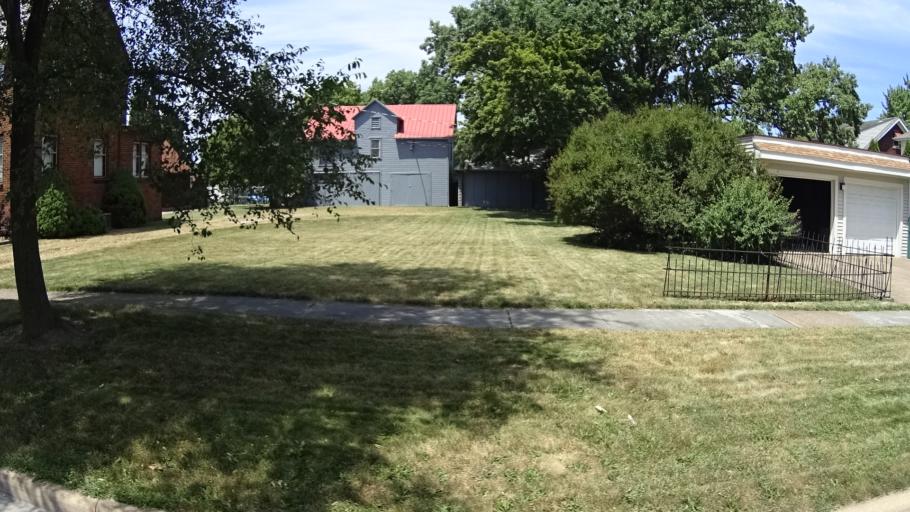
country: US
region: Ohio
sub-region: Erie County
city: Sandusky
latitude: 41.4471
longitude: -82.7050
